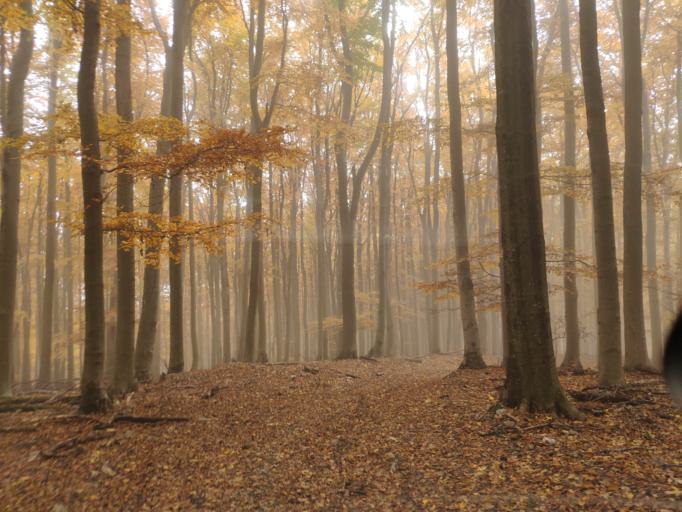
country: SK
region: Kosicky
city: Moldava nad Bodvou
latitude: 48.7306
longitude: 21.0142
